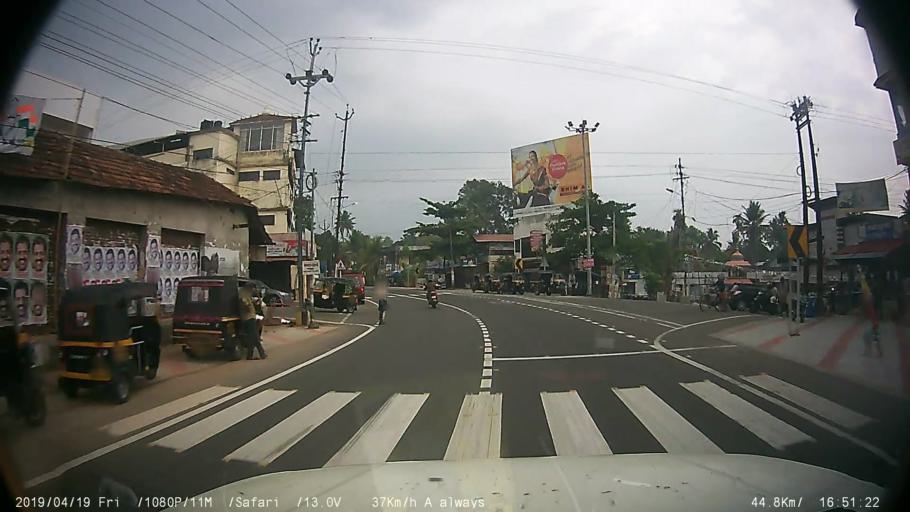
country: IN
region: Kerala
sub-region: Kottayam
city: Changanacheri
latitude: 9.4575
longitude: 76.5335
